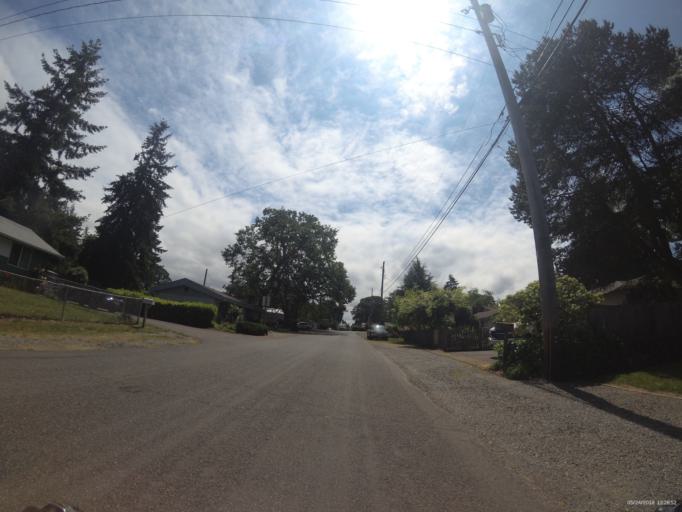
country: US
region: Washington
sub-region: Pierce County
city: Lakewood
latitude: 47.1803
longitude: -122.5277
